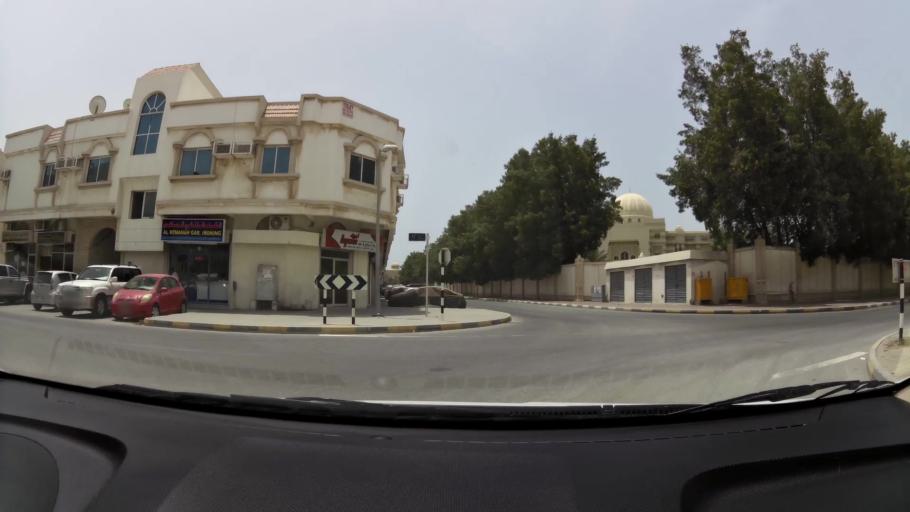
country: AE
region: Ash Shariqah
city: Sharjah
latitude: 25.3537
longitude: 55.4052
